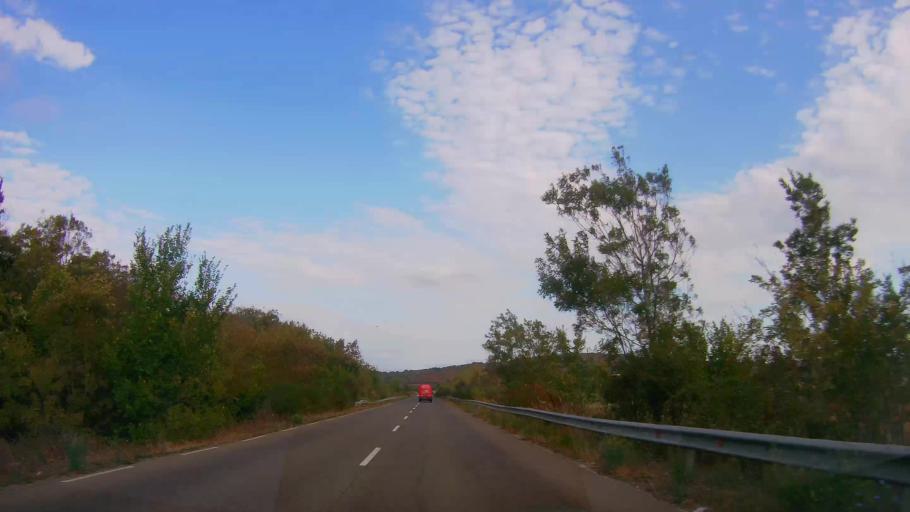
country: BG
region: Burgas
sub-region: Obshtina Sozopol
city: Sozopol
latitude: 42.3581
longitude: 27.7033
